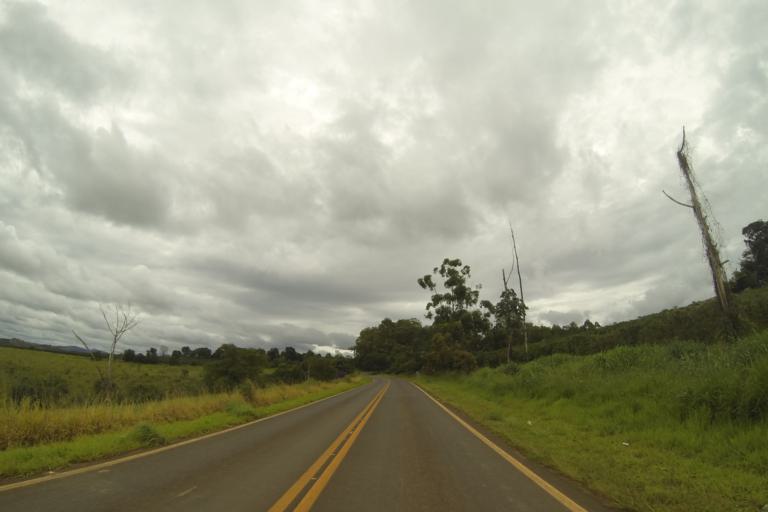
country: BR
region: Minas Gerais
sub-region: Bambui
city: Bambui
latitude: -20.0077
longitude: -46.2032
